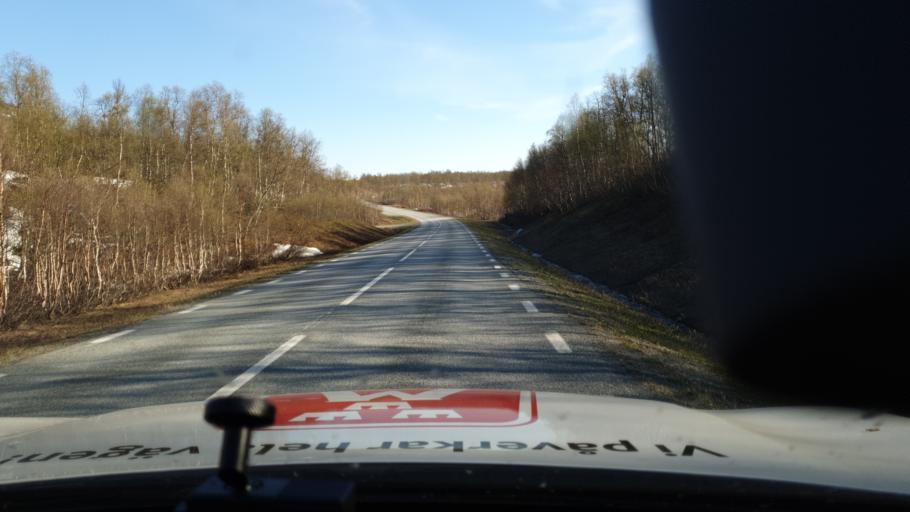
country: NO
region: Nordland
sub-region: Rana
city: Mo i Rana
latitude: 65.8931
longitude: 14.9842
